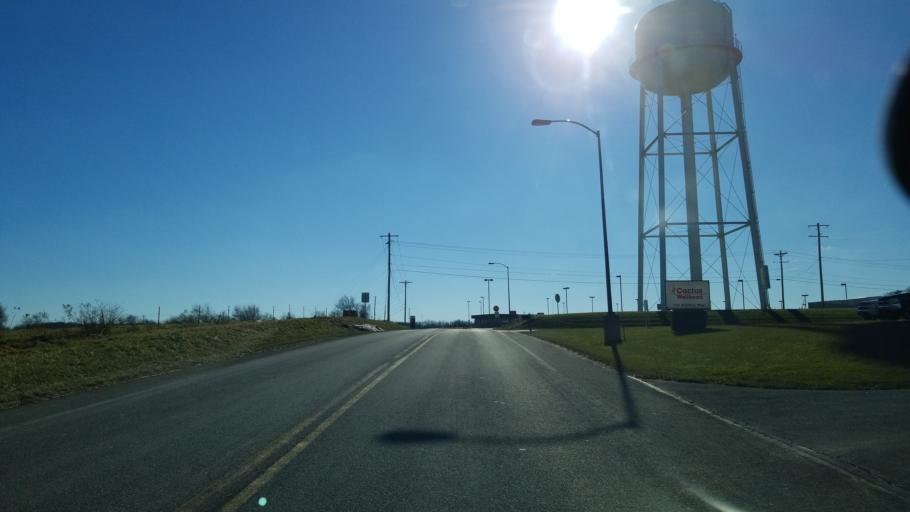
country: US
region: Pennsylvania
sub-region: Jefferson County
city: Reynoldsville
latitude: 41.1858
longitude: -78.8918
